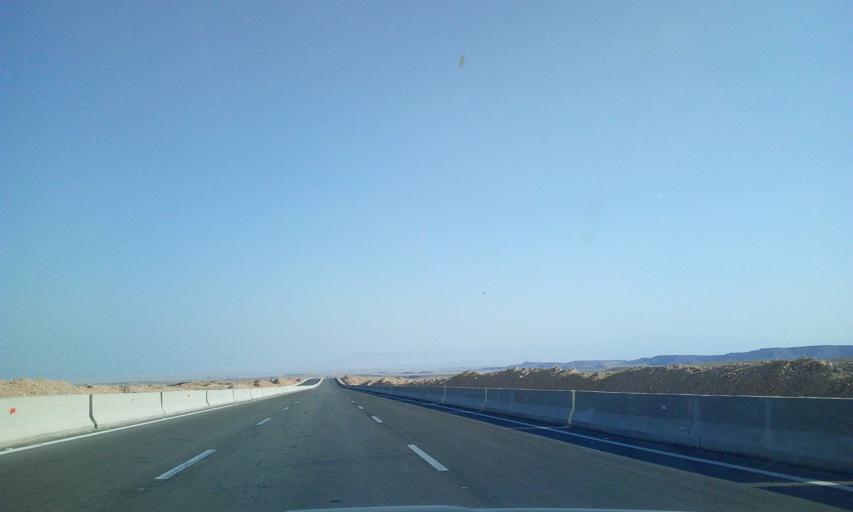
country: EG
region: As Suways
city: Ain Sukhna
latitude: 29.2665
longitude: 32.4719
